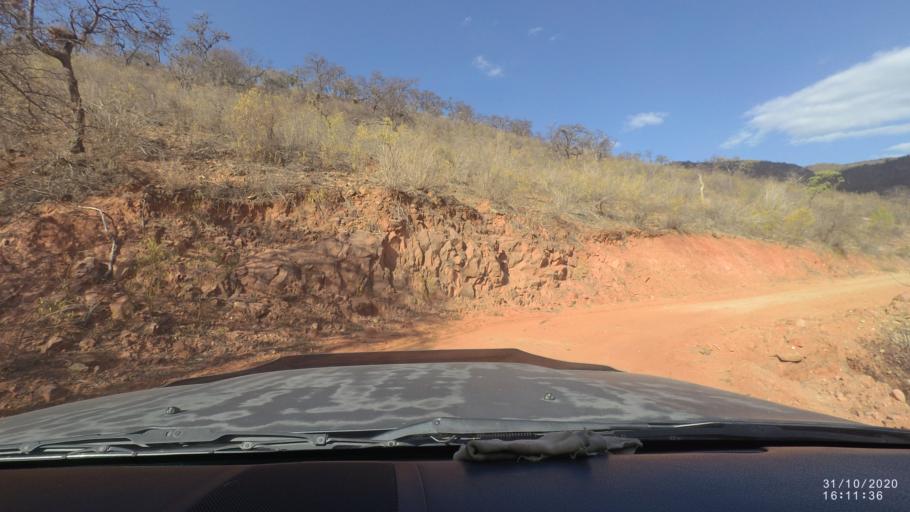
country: BO
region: Chuquisaca
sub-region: Provincia Zudanez
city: Mojocoya
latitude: -18.3791
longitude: -64.6235
